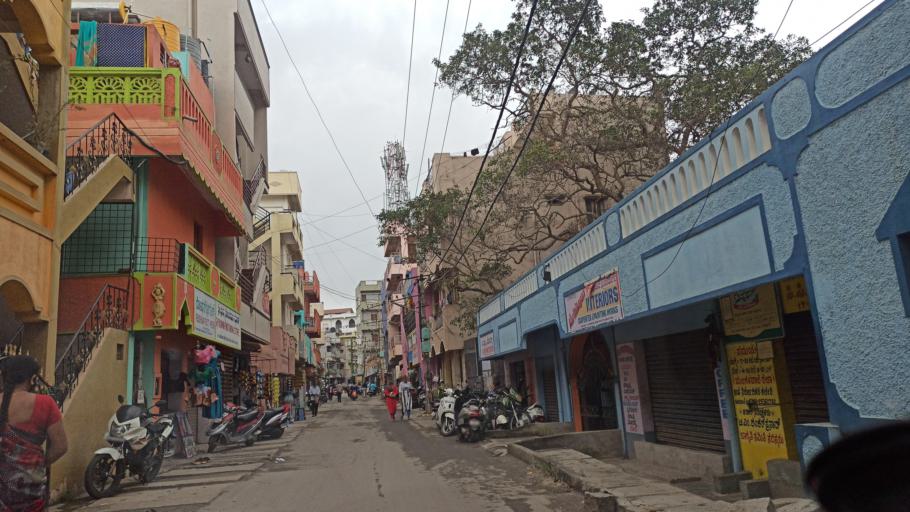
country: IN
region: Karnataka
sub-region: Bangalore Urban
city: Bangalore
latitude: 12.9947
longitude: 77.6752
